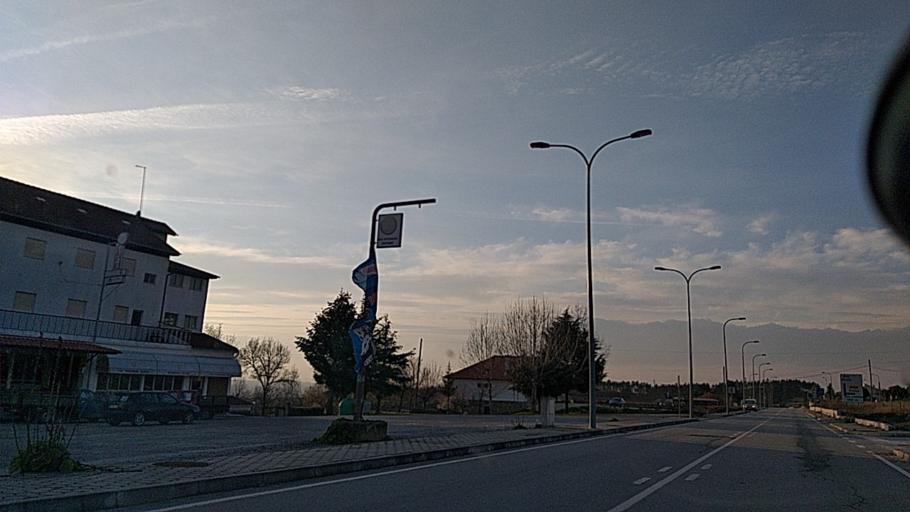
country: PT
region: Guarda
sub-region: Pinhel
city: Pinhel
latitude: 40.6016
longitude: -7.0001
